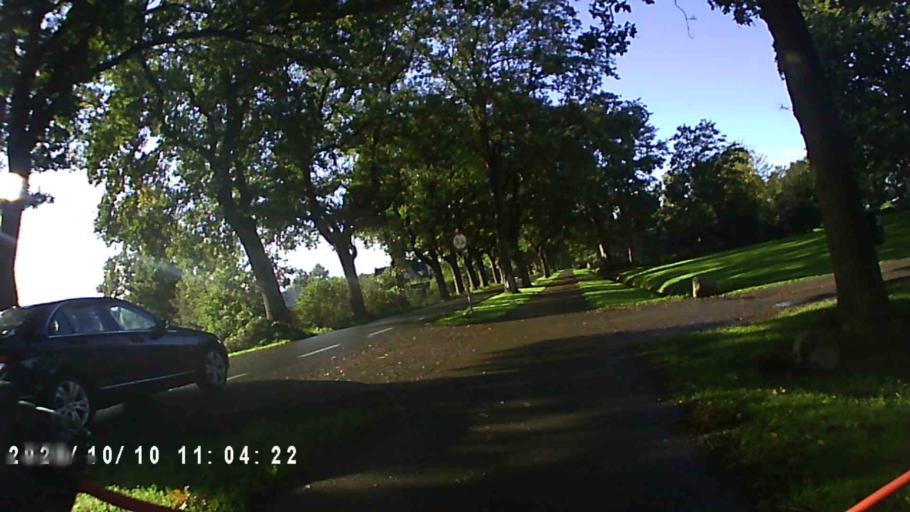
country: NL
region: Friesland
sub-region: Gemeente Achtkarspelen
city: Surhuisterveen
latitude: 53.1317
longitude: 6.2248
